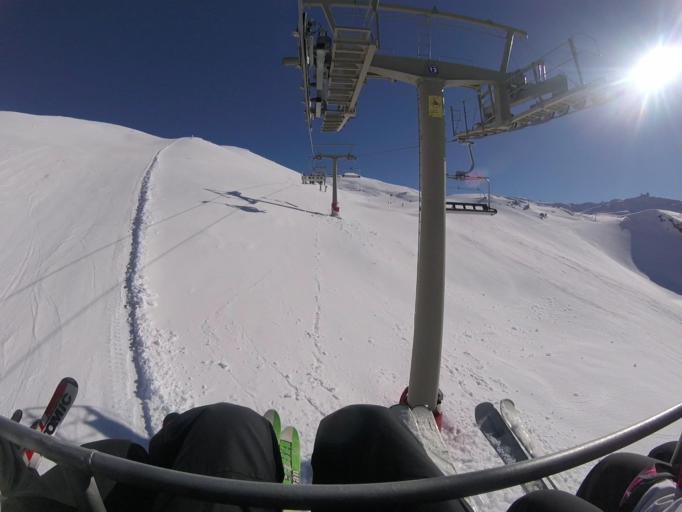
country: ES
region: Andalusia
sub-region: Provincia de Granada
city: Guejar-Sierra
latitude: 37.0722
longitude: -3.3831
